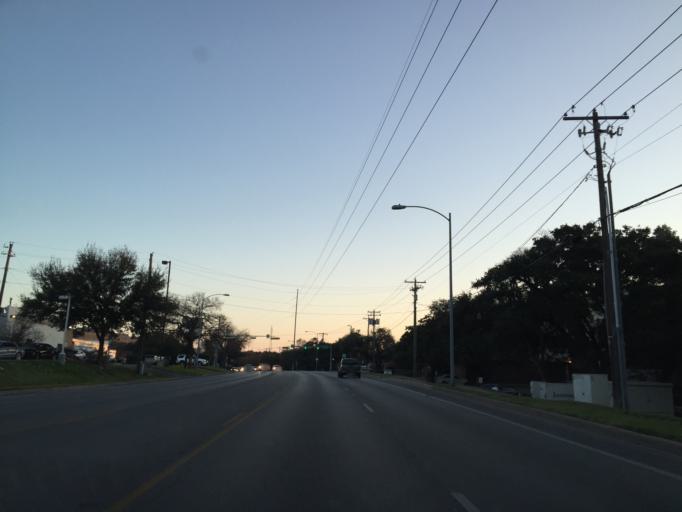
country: US
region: Texas
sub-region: Williamson County
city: Jollyville
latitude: 30.4090
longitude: -97.7478
